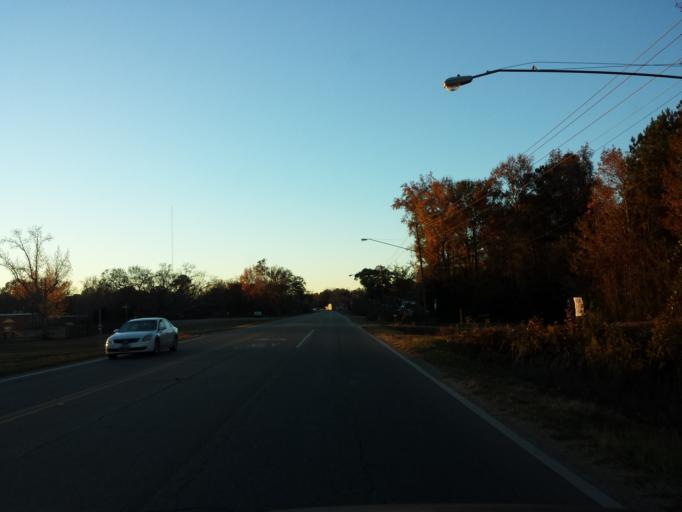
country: US
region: Mississippi
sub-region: Forrest County
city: Hattiesburg
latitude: 31.3419
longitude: -89.2905
